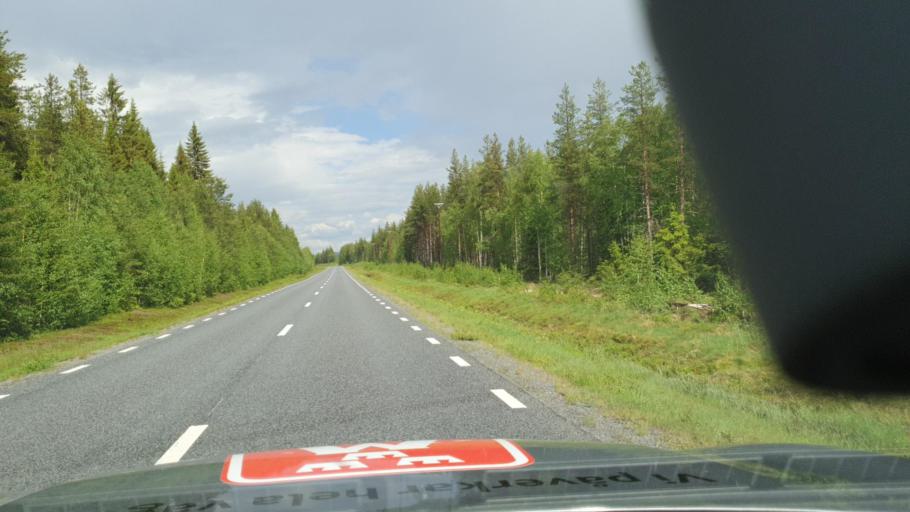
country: SE
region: Vaesterbotten
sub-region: Asele Kommun
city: Asele
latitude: 63.9245
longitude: 17.2567
